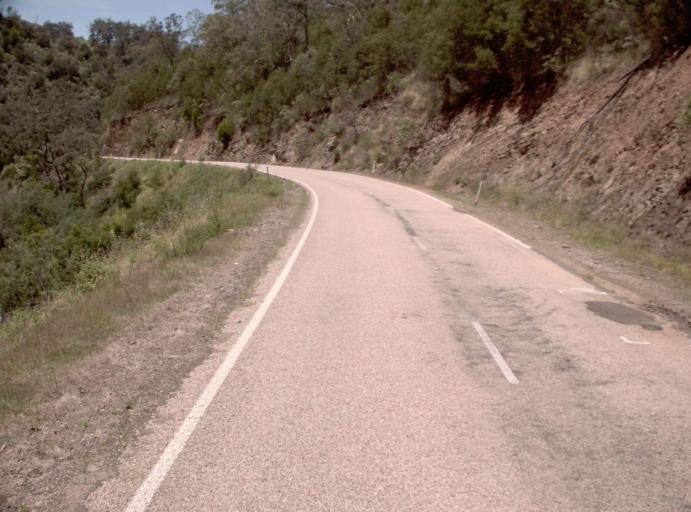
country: AU
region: Victoria
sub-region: East Gippsland
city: Lakes Entrance
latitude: -37.5277
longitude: 147.8506
